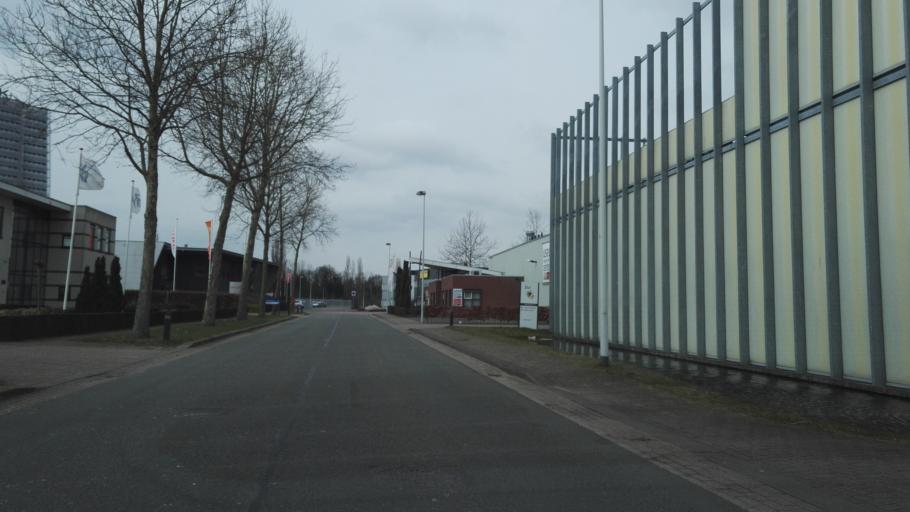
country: NL
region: Gelderland
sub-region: Gemeente Apeldoorn
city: Apeldoorn
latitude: 52.2390
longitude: 5.9849
